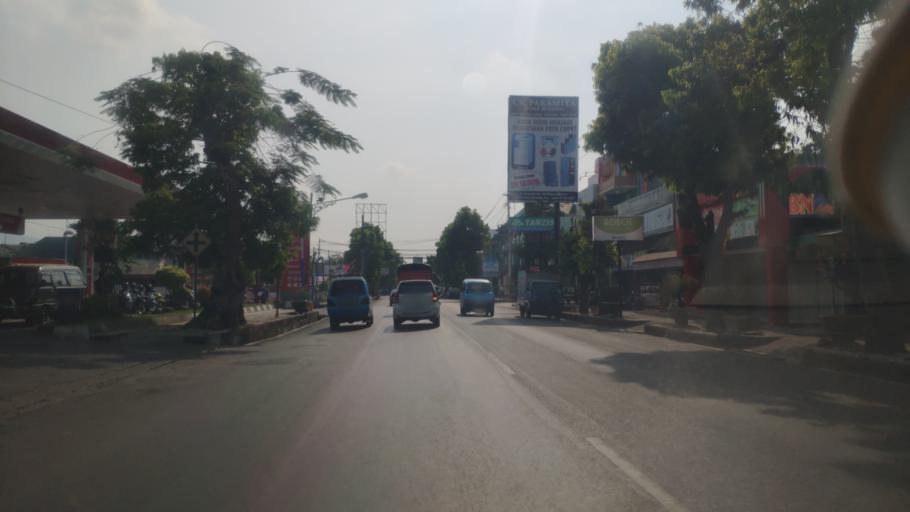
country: ID
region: Central Java
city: Wonosobo
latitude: -7.3968
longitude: 109.6976
